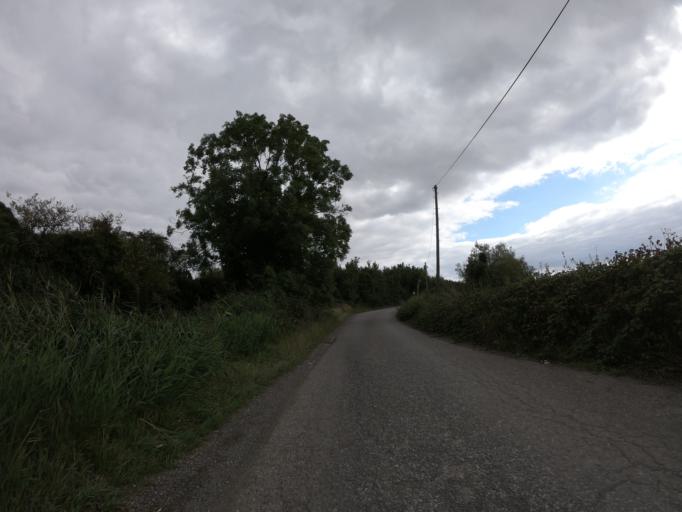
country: GB
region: England
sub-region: Kent
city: Dartford
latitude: 51.4674
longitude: 0.2163
